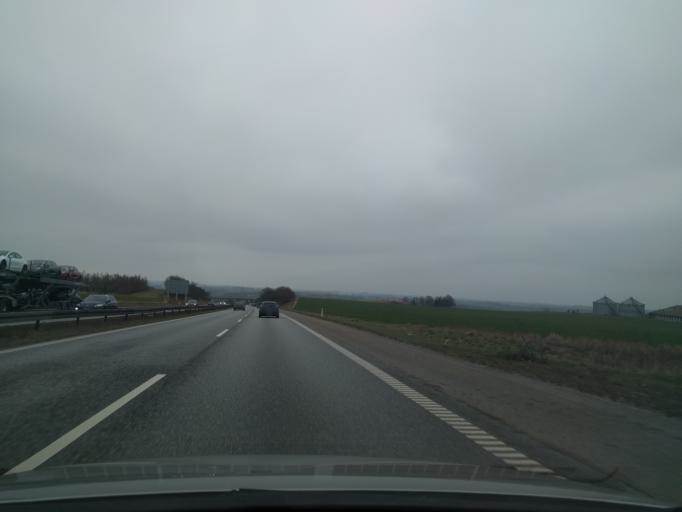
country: DK
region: Zealand
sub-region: Soro Kommune
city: Soro
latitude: 55.4233
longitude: 11.4566
